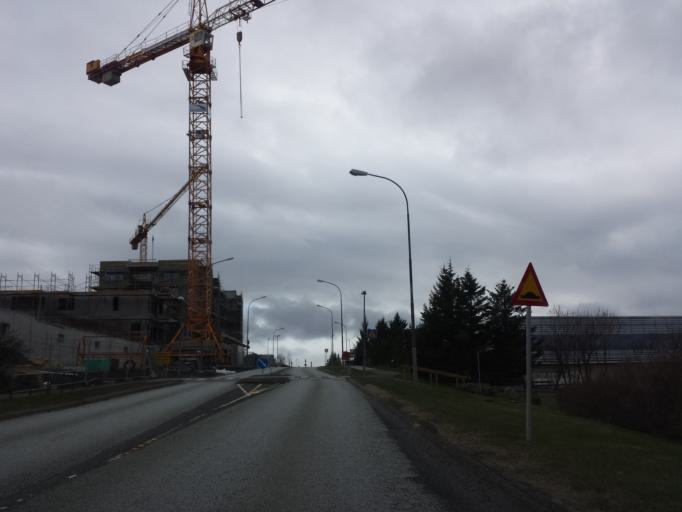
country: IS
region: Capital Region
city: Gardabaer
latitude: 64.0901
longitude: -21.9207
